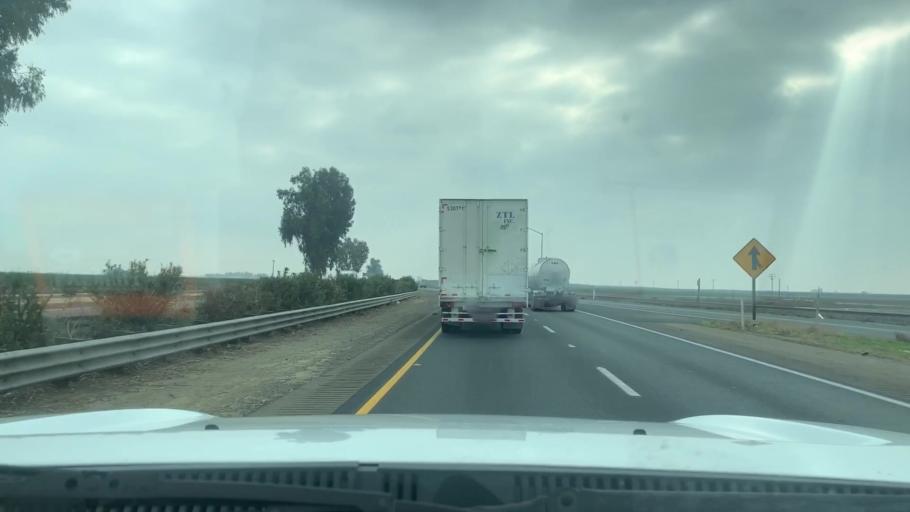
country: US
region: California
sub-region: Tulare County
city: Tipton
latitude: 36.0471
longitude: -119.3115
